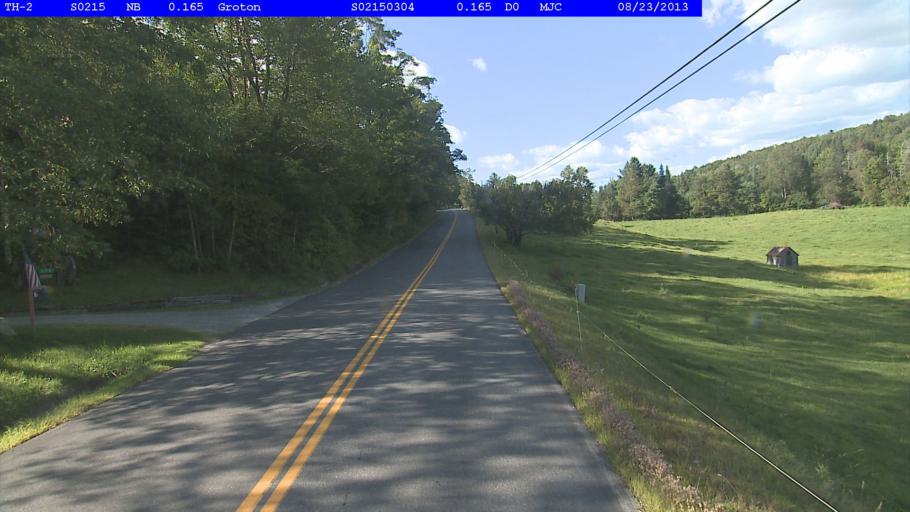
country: US
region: New Hampshire
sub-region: Grafton County
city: Woodsville
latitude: 44.2114
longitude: -72.1907
